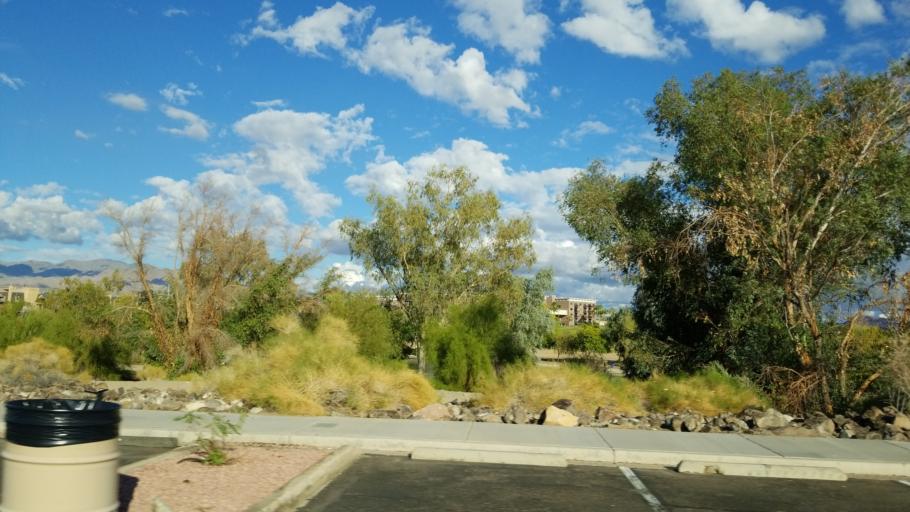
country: US
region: Arizona
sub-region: Mohave County
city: Lake Havasu City
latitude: 34.4688
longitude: -114.3490
